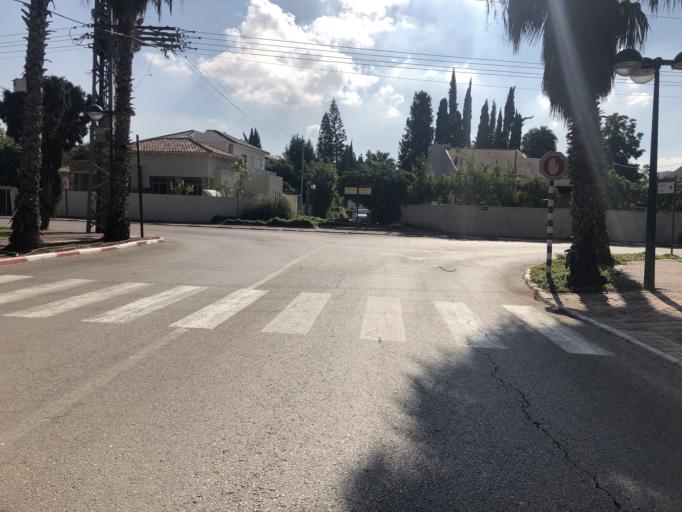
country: IL
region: Tel Aviv
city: Or Yehuda
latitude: 32.0327
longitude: 34.8708
